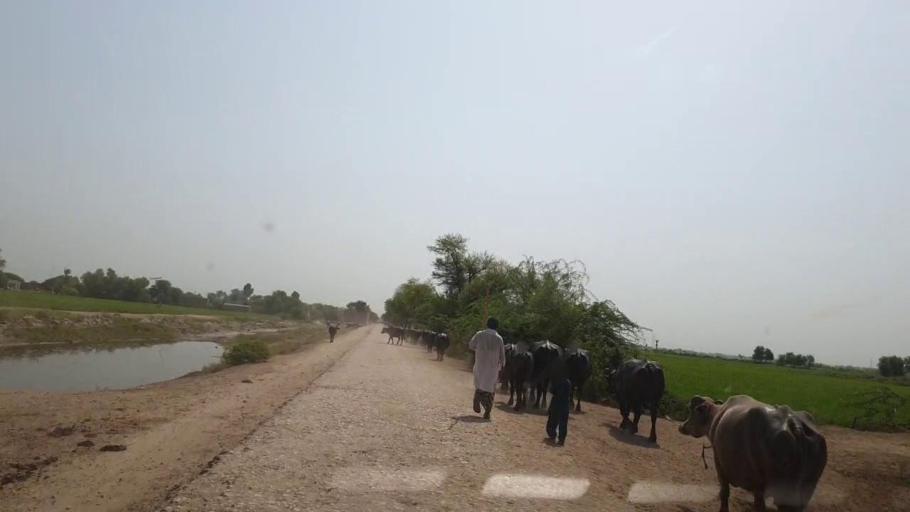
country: PK
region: Sindh
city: Lakhi
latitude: 27.8786
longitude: 68.6607
